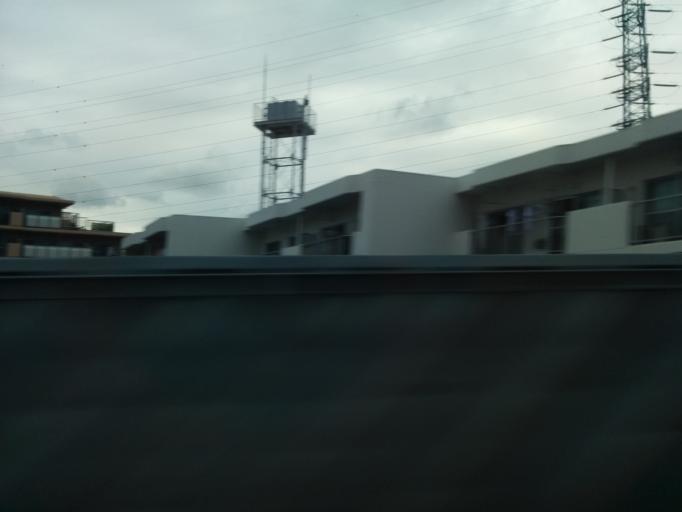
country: JP
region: Kanagawa
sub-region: Kawasaki-shi
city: Kawasaki
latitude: 35.5303
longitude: 139.6388
